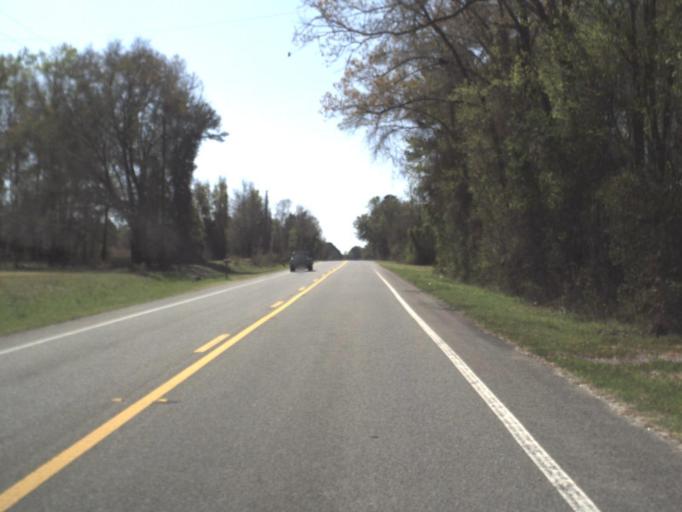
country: US
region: Florida
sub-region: Jefferson County
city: Monticello
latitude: 30.5108
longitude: -84.0243
